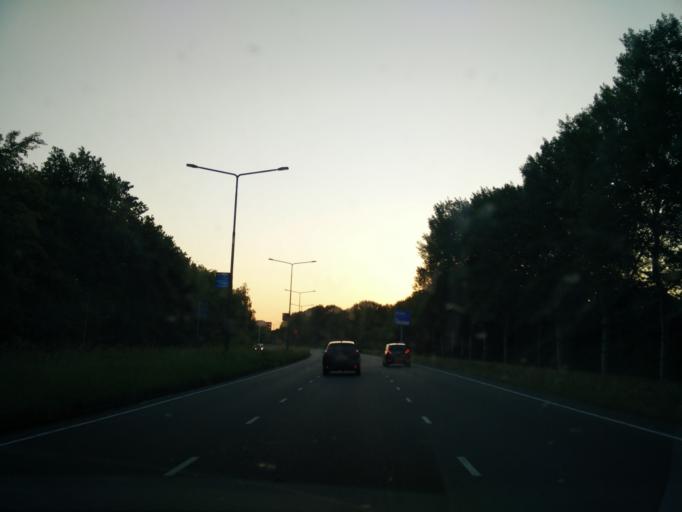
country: NL
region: North Brabant
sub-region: Gemeente Breda
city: Breda
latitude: 51.6016
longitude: 4.7366
